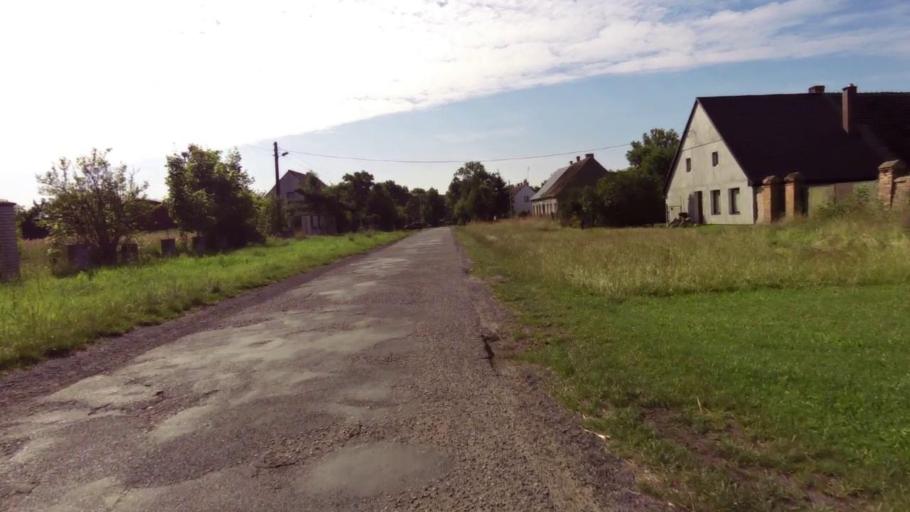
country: PL
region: West Pomeranian Voivodeship
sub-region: Powiat stargardzki
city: Marianowo
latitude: 53.3437
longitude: 15.1925
